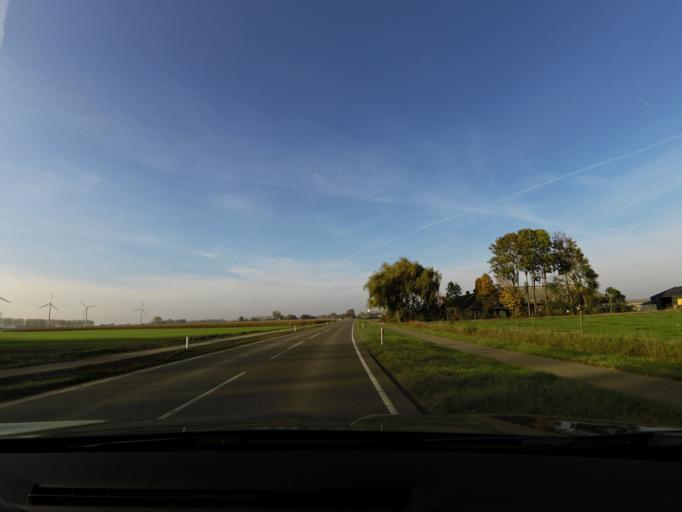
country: NL
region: North Brabant
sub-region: Gemeente Moerdijk
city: Klundert
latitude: 51.6150
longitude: 4.6443
